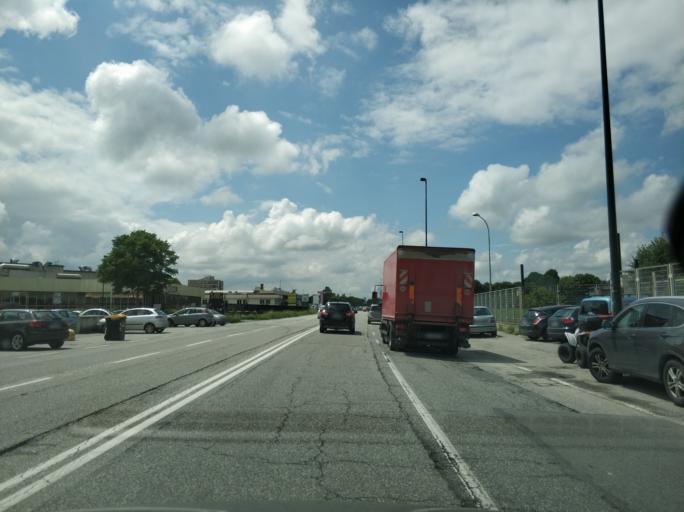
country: IT
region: Piedmont
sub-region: Provincia di Torino
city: Settimo Torinese
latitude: 45.1205
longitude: 7.7420
